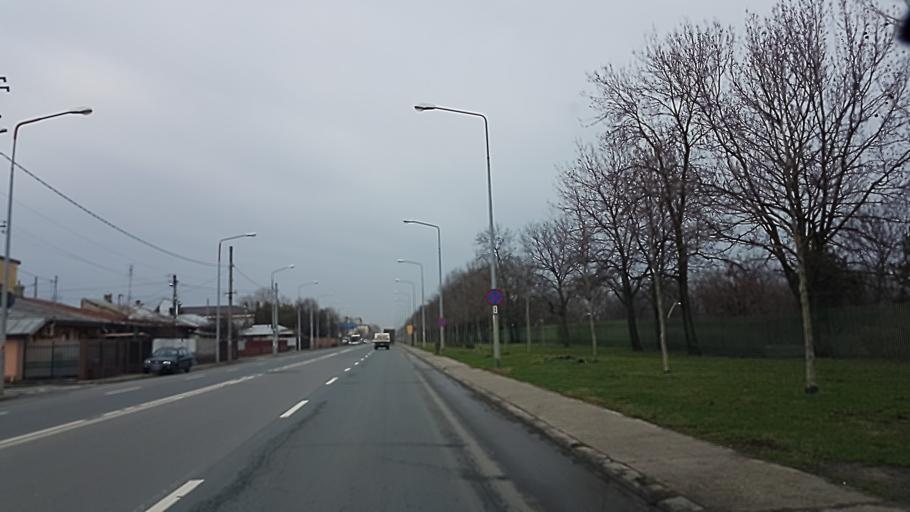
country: RO
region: Ilfov
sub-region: Comuna Pantelimon
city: Pantelimon
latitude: 44.4350
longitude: 26.2035
